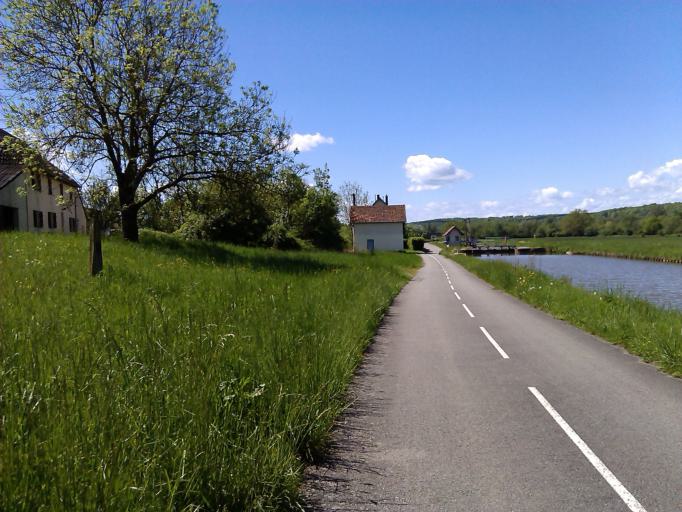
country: FR
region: Franche-Comte
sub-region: Territoire de Belfort
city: Morvillars
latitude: 47.5641
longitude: 6.9408
